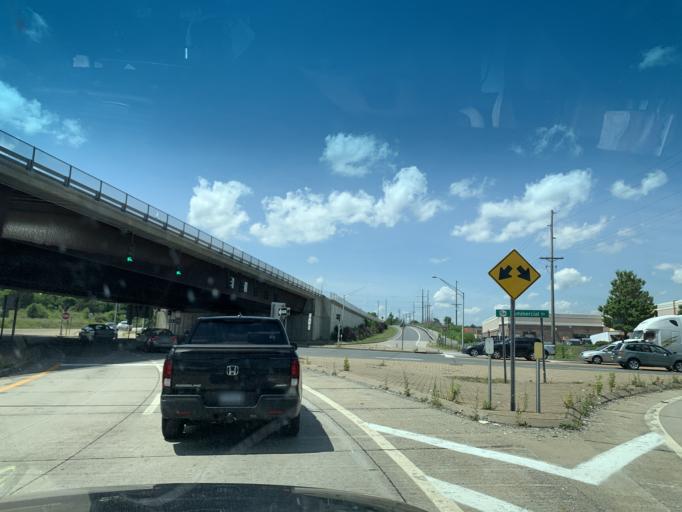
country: US
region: New York
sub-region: Oneida County
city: New York Mills
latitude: 43.0916
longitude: -75.3081
